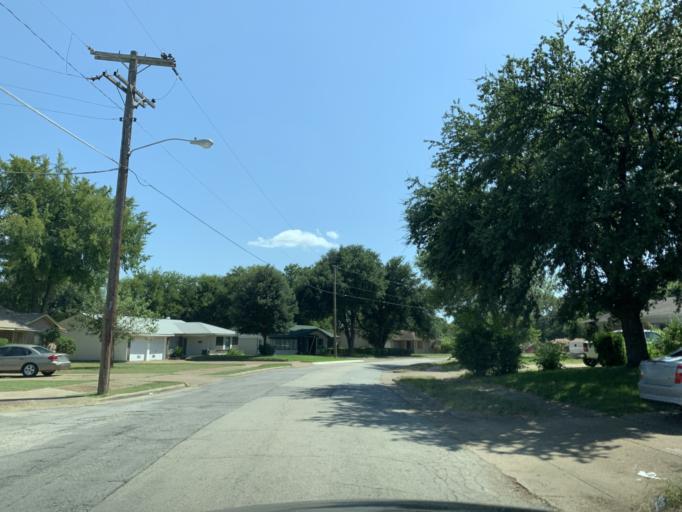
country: US
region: Texas
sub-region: Dallas County
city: Hutchins
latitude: 32.6741
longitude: -96.8010
